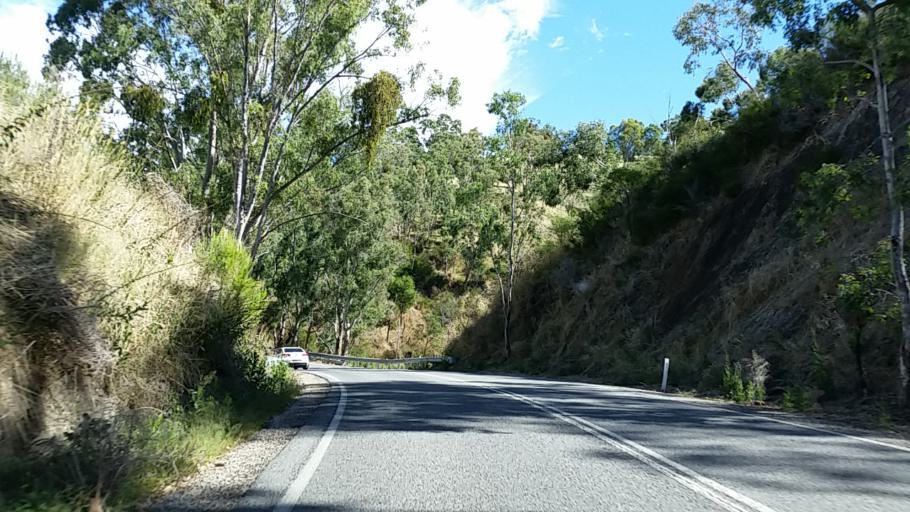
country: AU
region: South Australia
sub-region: Tea Tree Gully
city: Golden Grove
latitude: -34.8507
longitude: 138.7912
